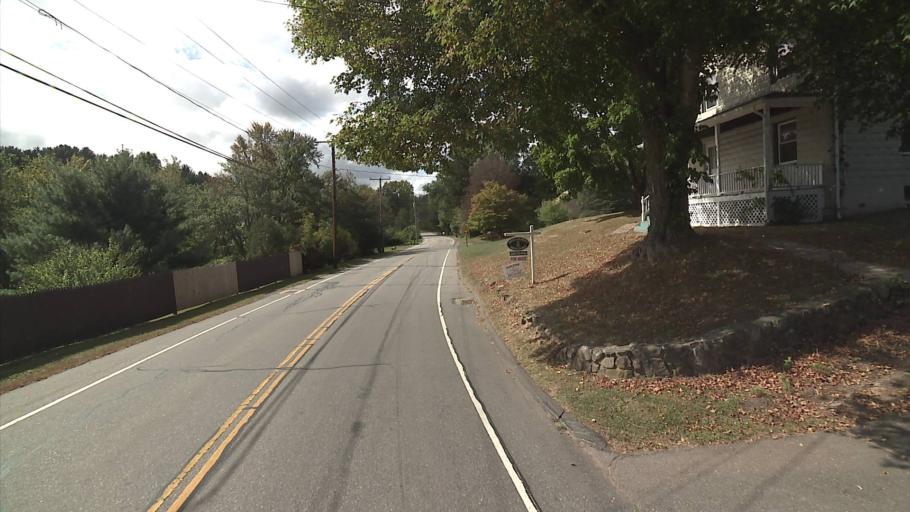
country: US
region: Connecticut
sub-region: Middlesex County
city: Durham
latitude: 41.5261
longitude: -72.7008
